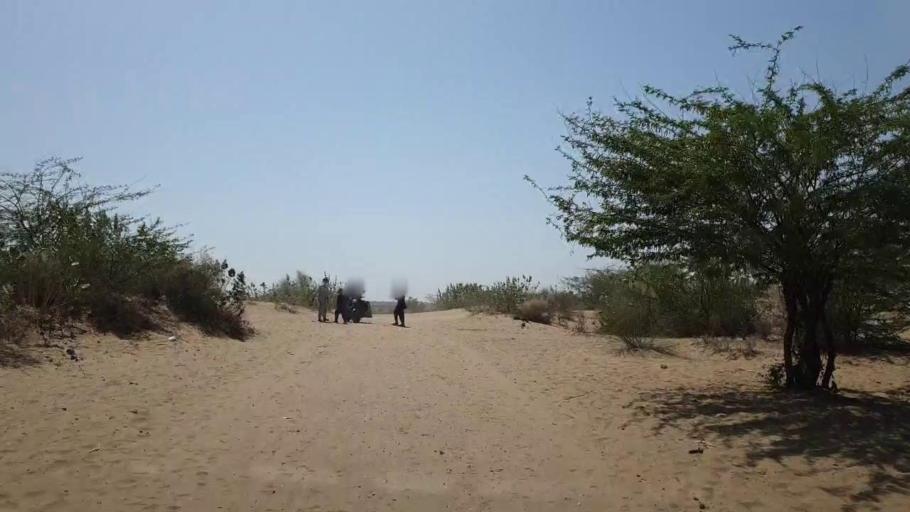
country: PK
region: Sindh
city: Umarkot
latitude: 25.1902
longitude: 69.8896
